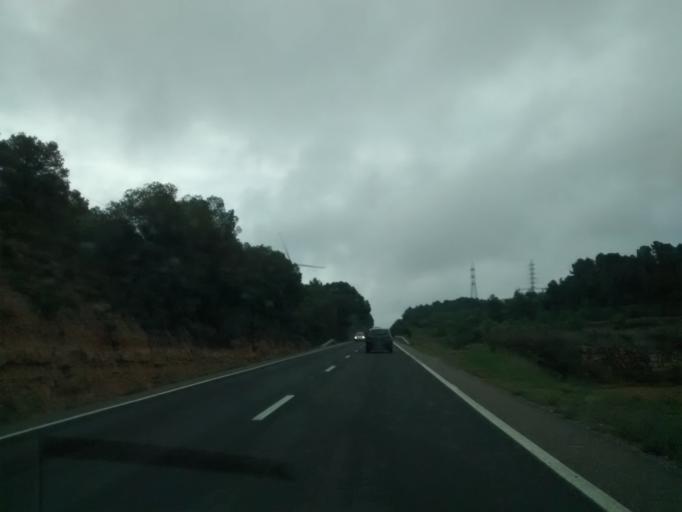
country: ES
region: Catalonia
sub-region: Provincia de Tarragona
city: Batea
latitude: 41.0604
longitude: 0.3532
